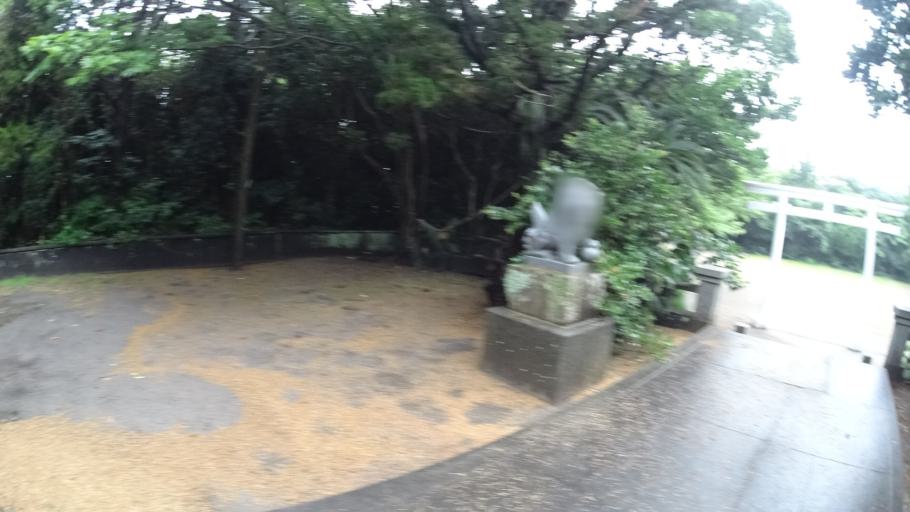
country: JP
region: Shizuoka
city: Shimoda
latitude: 34.3338
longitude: 139.2130
